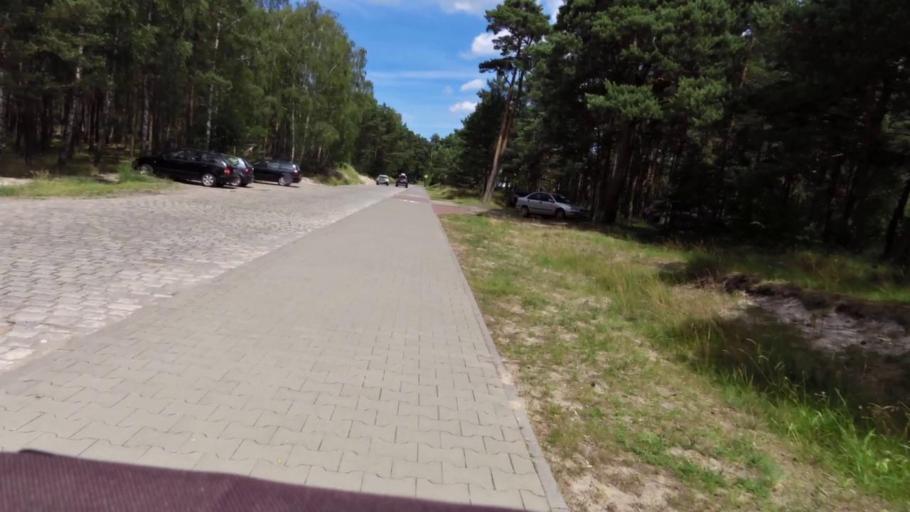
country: PL
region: West Pomeranian Voivodeship
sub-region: Powiat gryficki
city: Mrzezyno
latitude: 54.1378
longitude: 15.2752
